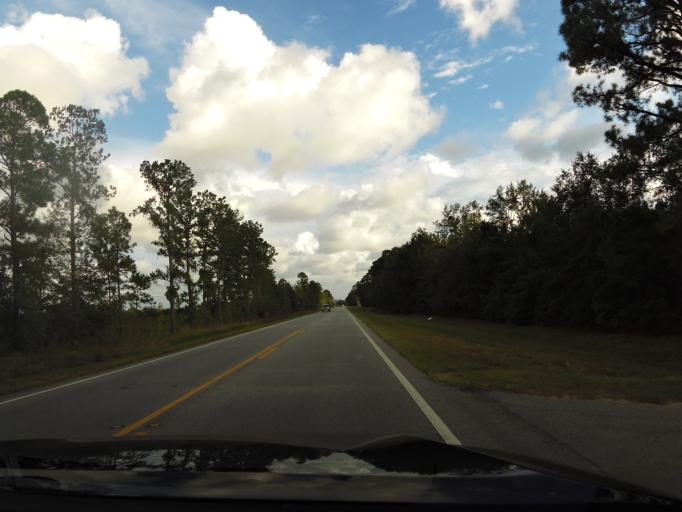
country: US
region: Georgia
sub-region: Liberty County
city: Midway
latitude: 31.7643
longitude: -81.4478
